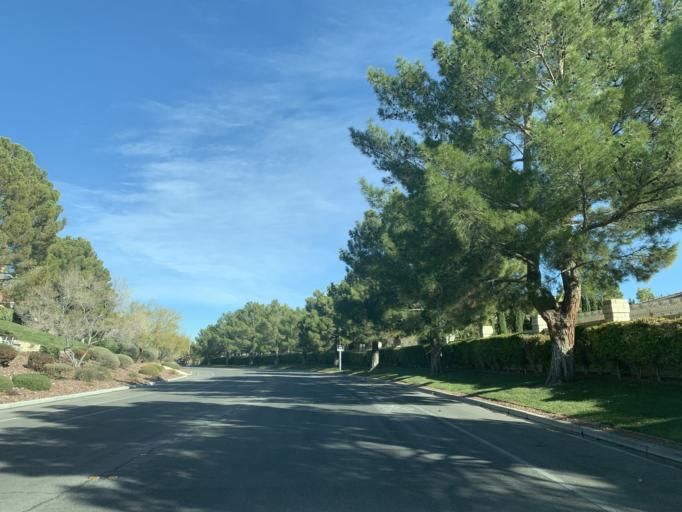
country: US
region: Nevada
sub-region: Clark County
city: Summerlin South
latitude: 36.1354
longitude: -115.2898
